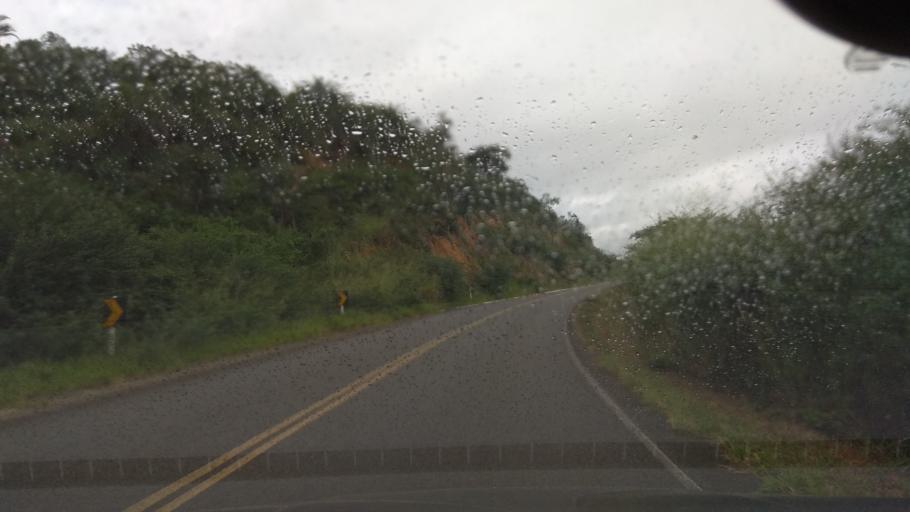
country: BR
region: Bahia
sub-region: Ubaira
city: Ubaira
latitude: -13.2438
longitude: -39.7385
